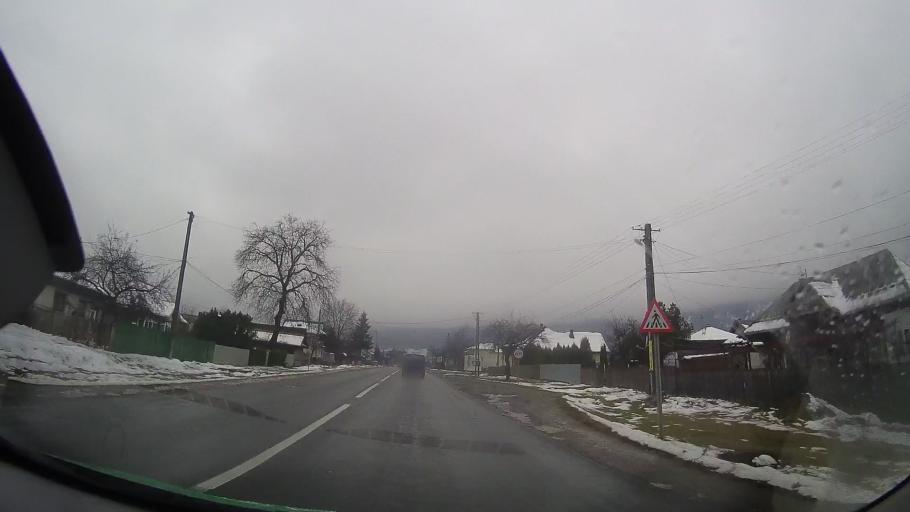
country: RO
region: Neamt
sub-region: Comuna Pangarati
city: Stejaru
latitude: 46.9136
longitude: 26.1837
